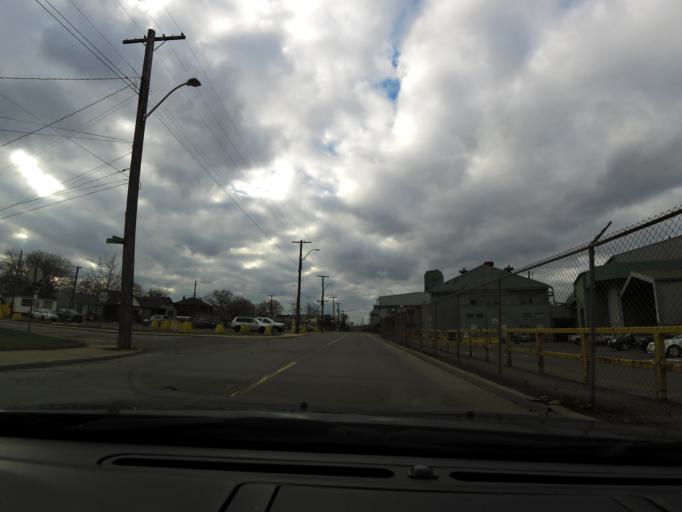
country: CA
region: Ontario
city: Hamilton
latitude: 43.2560
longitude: -79.8067
